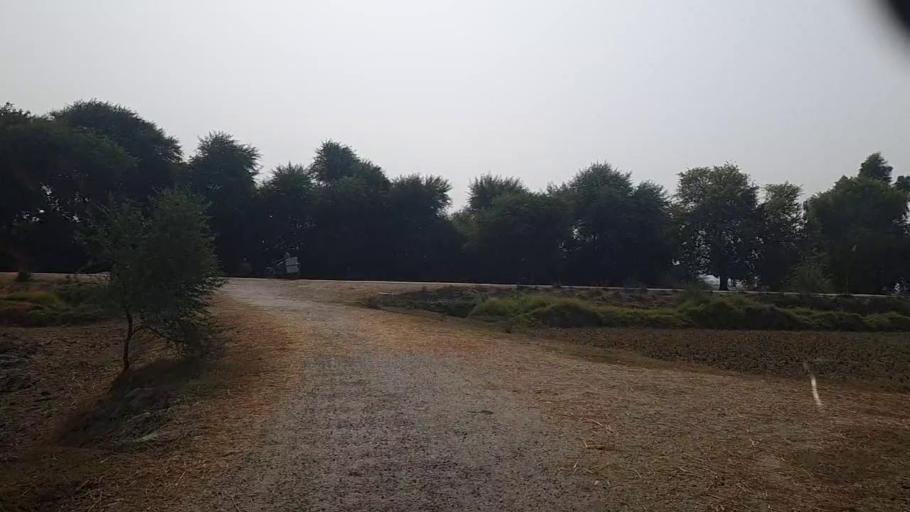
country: PK
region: Sindh
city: Kashmor
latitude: 28.3781
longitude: 69.4465
